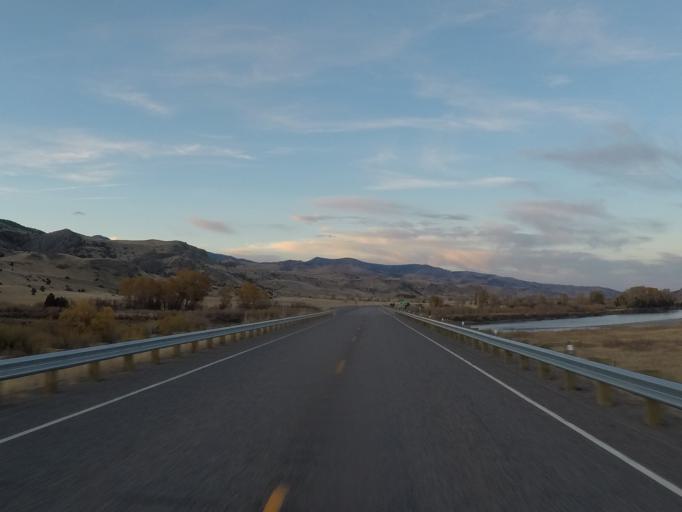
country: US
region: Montana
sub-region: Gallatin County
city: Bozeman
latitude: 45.2522
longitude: -110.8682
